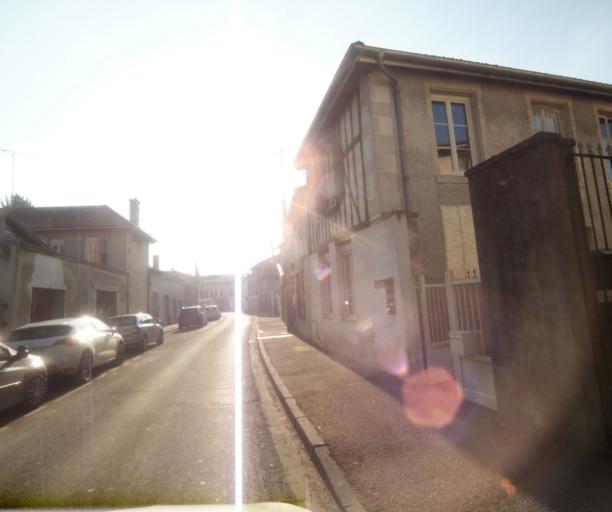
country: FR
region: Champagne-Ardenne
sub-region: Departement de la Haute-Marne
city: Wassy
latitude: 48.4996
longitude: 4.9456
